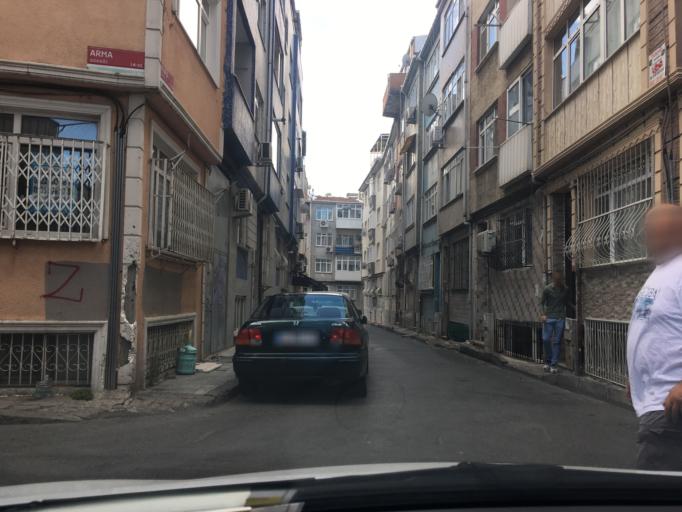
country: TR
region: Istanbul
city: Istanbul
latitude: 41.0155
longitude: 28.9270
